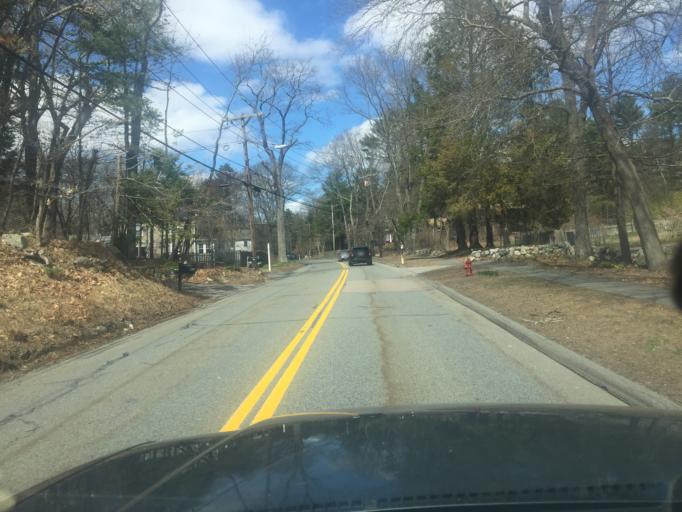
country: US
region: Massachusetts
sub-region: Norfolk County
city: Norfolk
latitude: 42.1135
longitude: -71.3185
